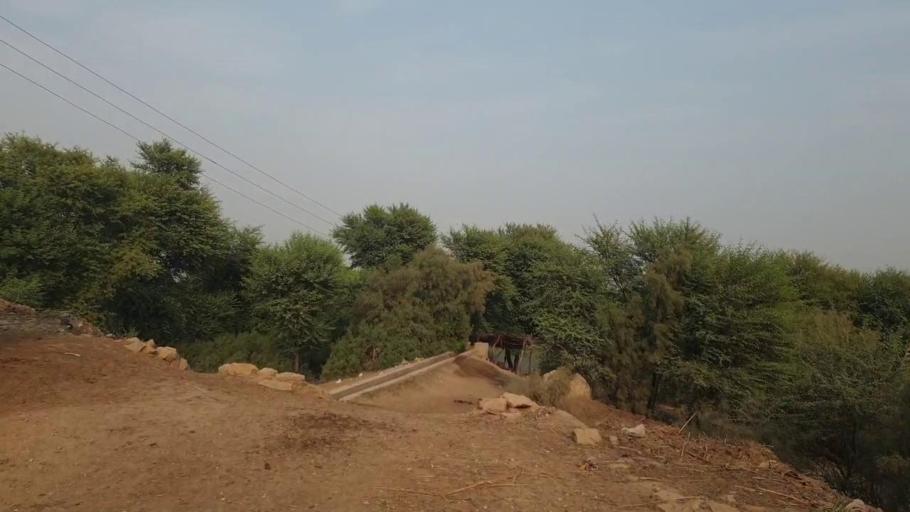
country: PK
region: Sindh
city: Sann
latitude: 26.1280
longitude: 68.0647
